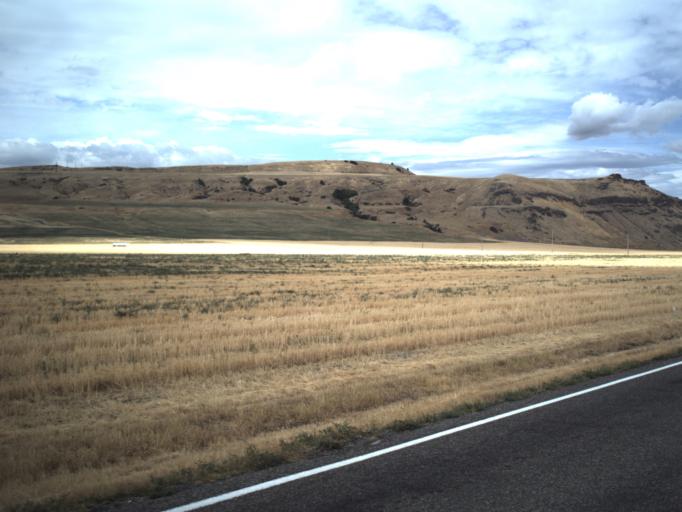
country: US
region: Utah
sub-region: Cache County
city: Benson
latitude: 41.7781
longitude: -111.9846
